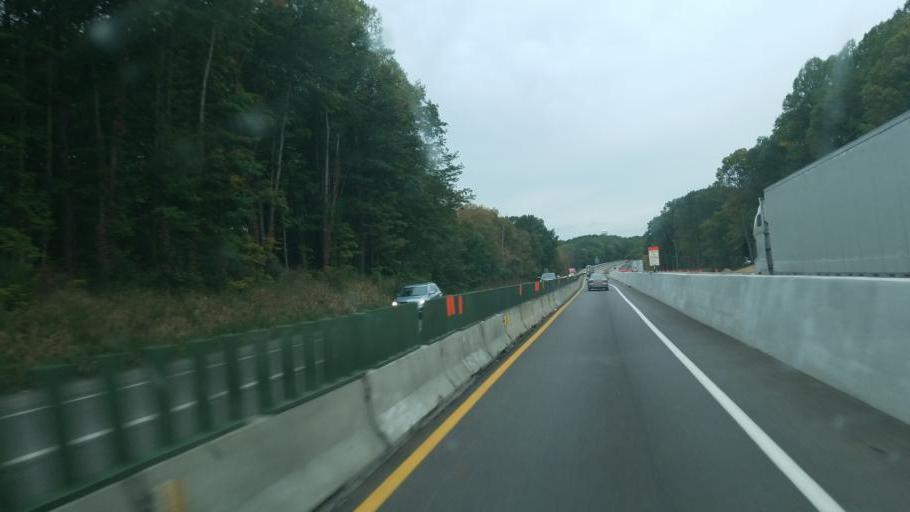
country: US
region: Ohio
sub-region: Summit County
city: Norton
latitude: 41.0402
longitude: -81.6758
